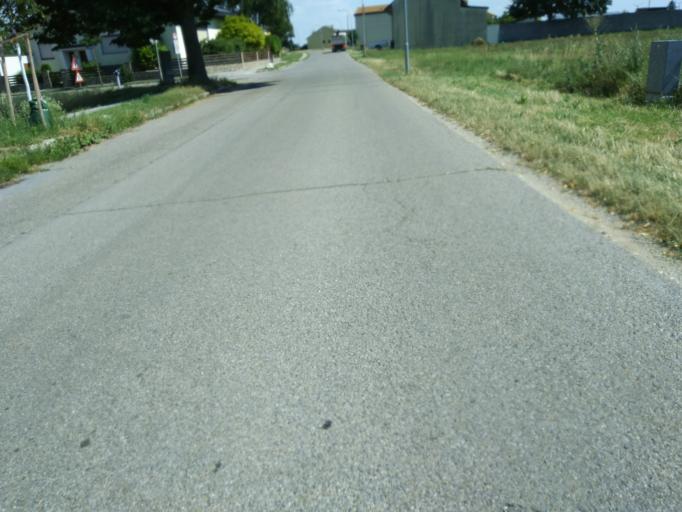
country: AT
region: Lower Austria
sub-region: Politischer Bezirk Mistelbach
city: Wolkersdorf im Weinviertel
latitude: 48.3740
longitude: 16.5162
